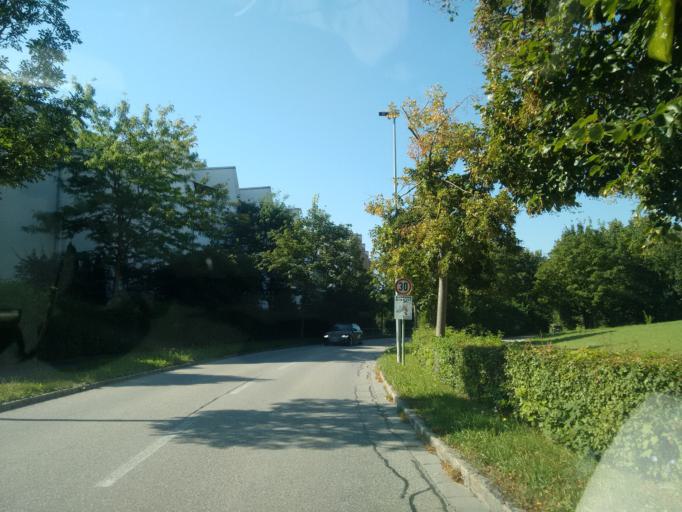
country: AT
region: Upper Austria
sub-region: Wels Stadt
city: Wels
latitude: 48.1618
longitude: 13.9933
